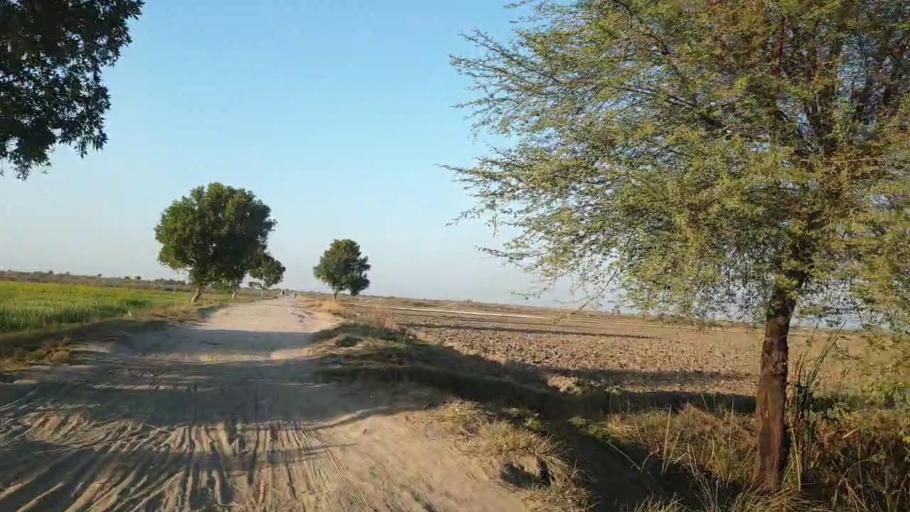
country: PK
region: Sindh
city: Mirpur Khas
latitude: 25.6711
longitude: 69.0480
